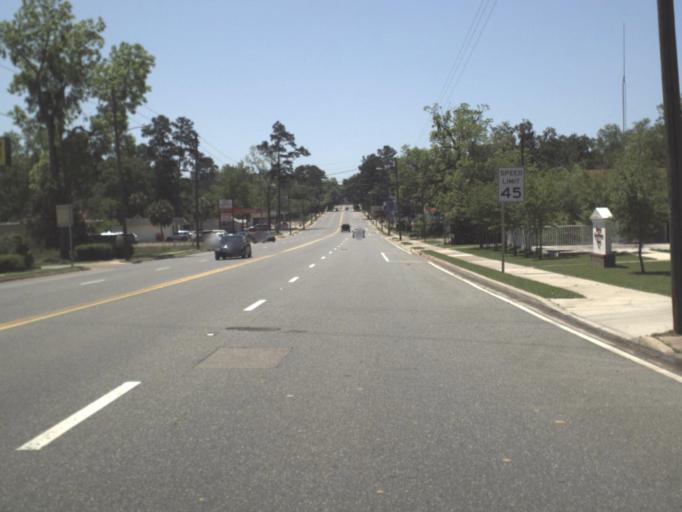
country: US
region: Florida
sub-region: Jefferson County
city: Monticello
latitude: 30.5550
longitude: -83.8703
